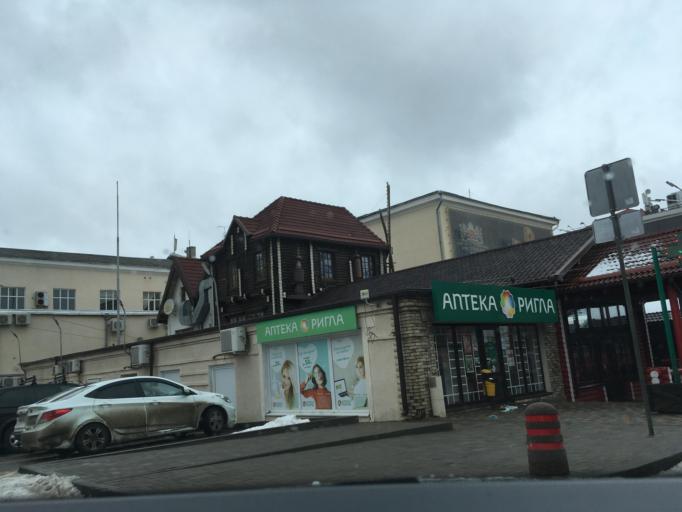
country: RU
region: Rostov
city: Rostov-na-Donu
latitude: 47.2590
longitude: 39.7189
